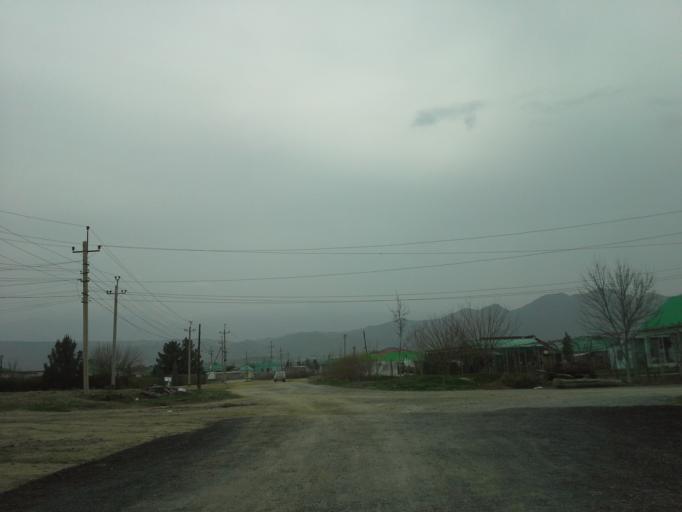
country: TM
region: Ahal
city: Abadan
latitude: 37.9775
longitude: 58.2266
